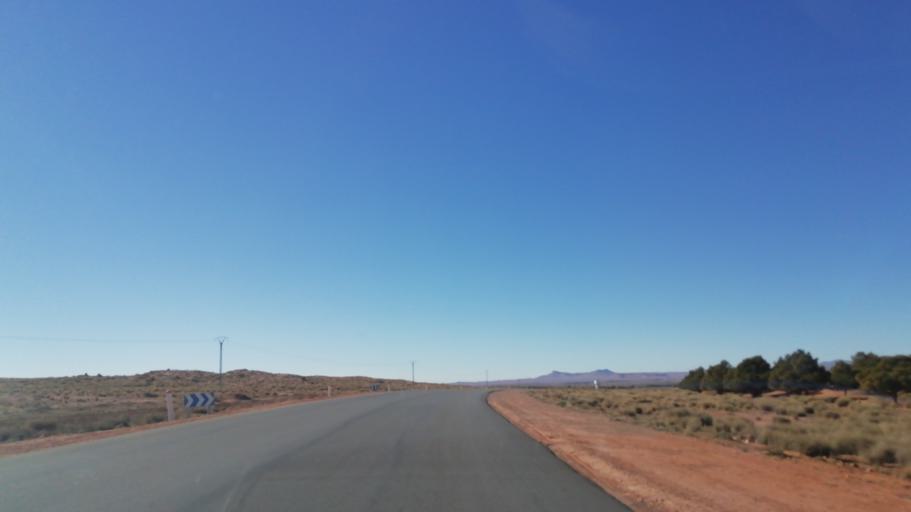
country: DZ
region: El Bayadh
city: El Bayadh
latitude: 33.6350
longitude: 1.3769
